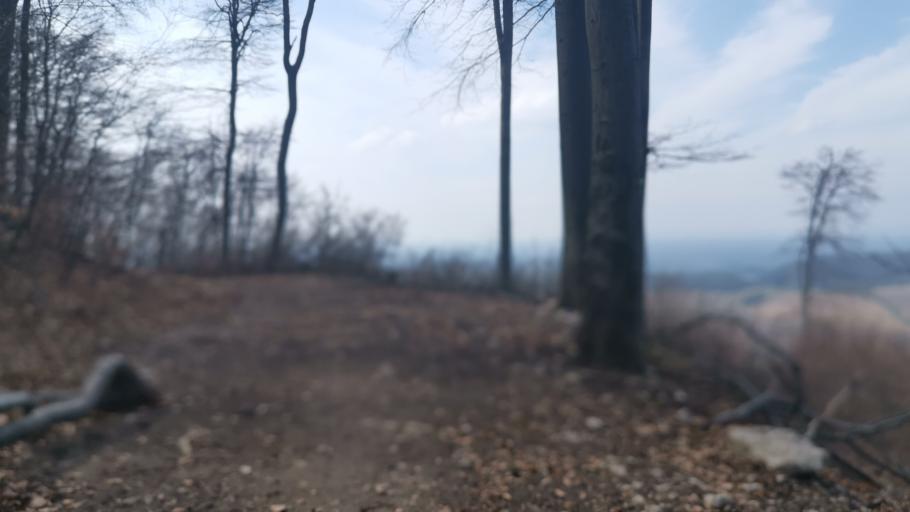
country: SK
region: Trnavsky
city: Smolenice
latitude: 48.5265
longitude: 17.3934
